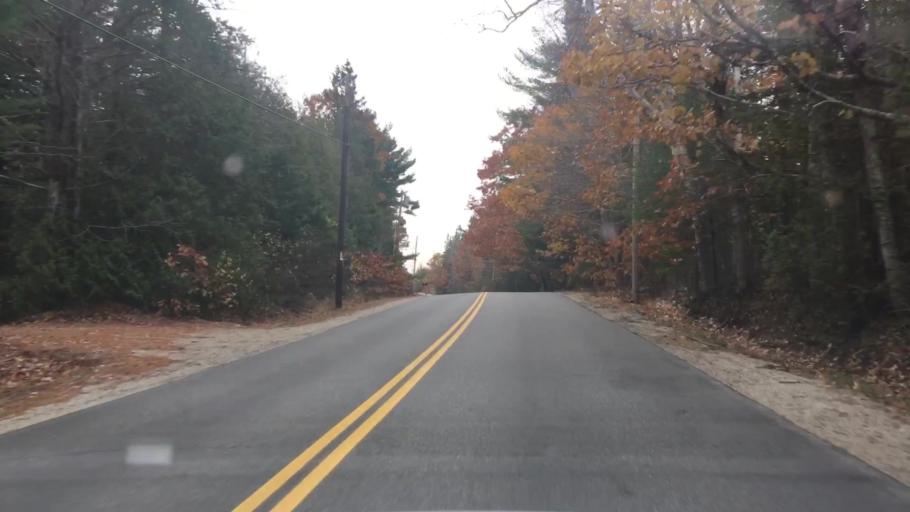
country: US
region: Maine
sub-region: Hancock County
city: Penobscot
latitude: 44.4585
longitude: -68.6378
